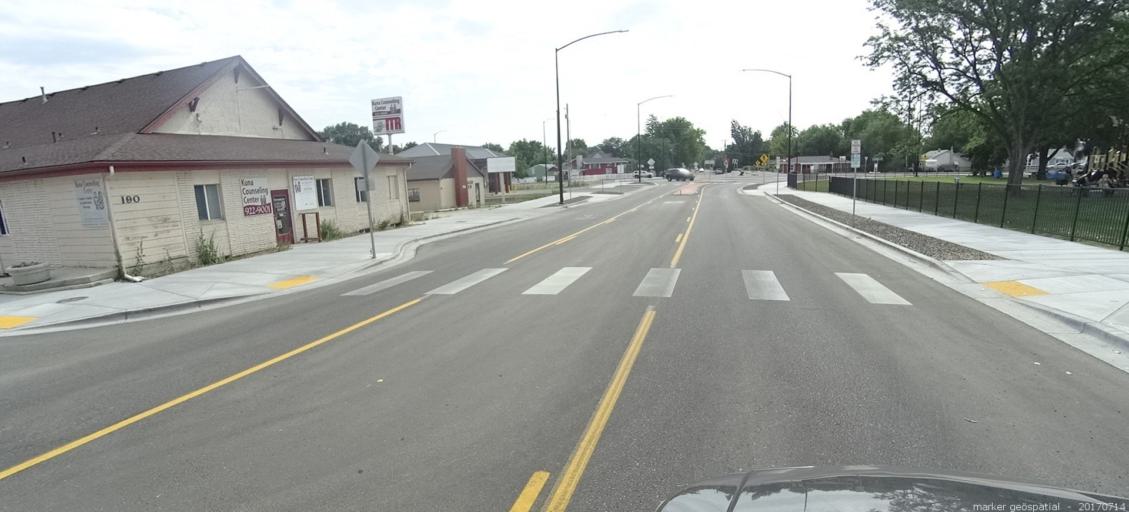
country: US
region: Idaho
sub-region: Ada County
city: Kuna
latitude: 43.4906
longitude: -116.4151
